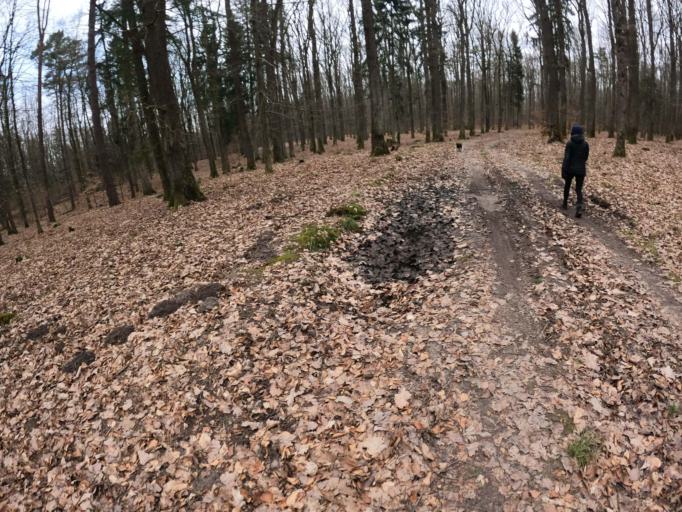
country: PL
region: West Pomeranian Voivodeship
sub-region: Powiat kamienski
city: Golczewo
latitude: 53.8100
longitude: 15.0180
